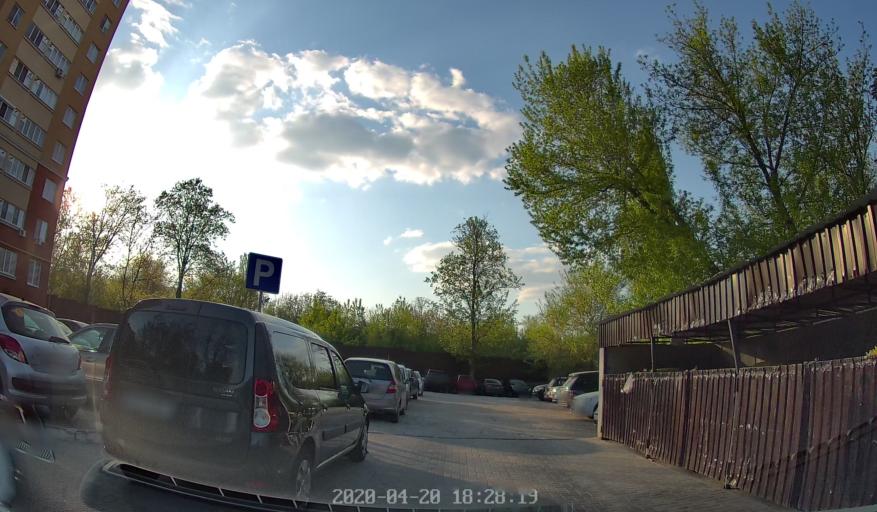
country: MD
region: Chisinau
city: Chisinau
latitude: 46.9907
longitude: 28.8333
